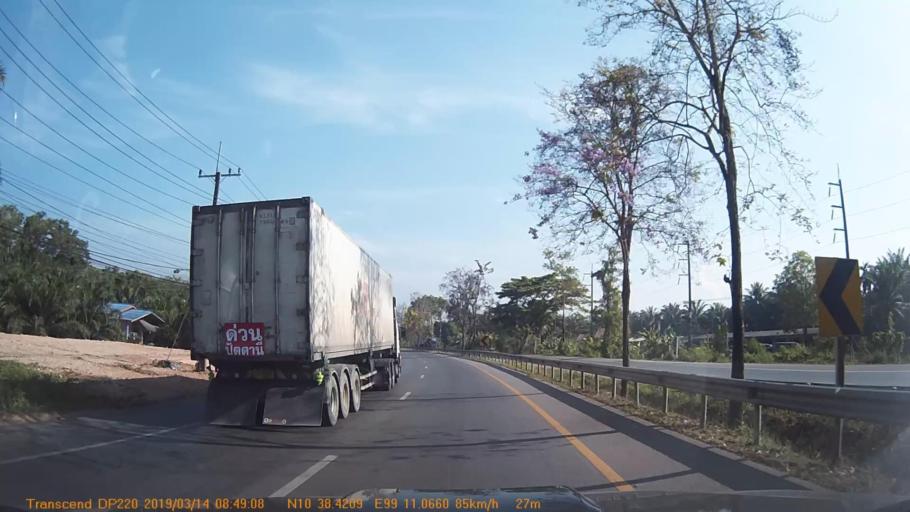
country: TH
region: Chumphon
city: Tha Sae
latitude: 10.6406
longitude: 99.1845
